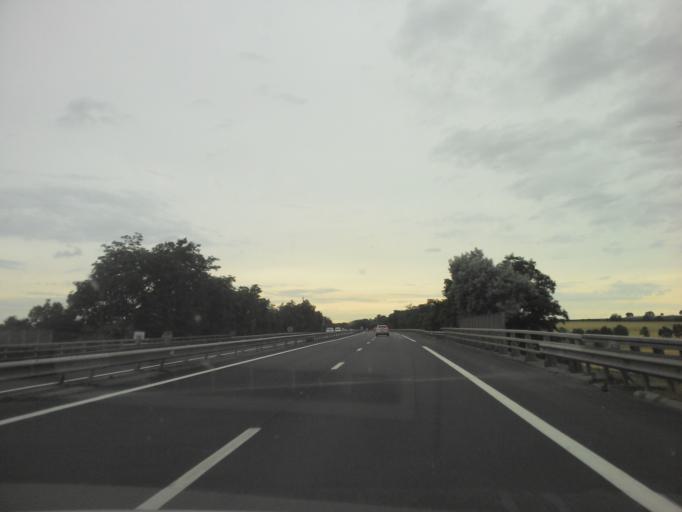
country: FR
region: Auvergne
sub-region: Departement du Puy-de-Dome
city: Riom
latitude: 45.9160
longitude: 3.1506
